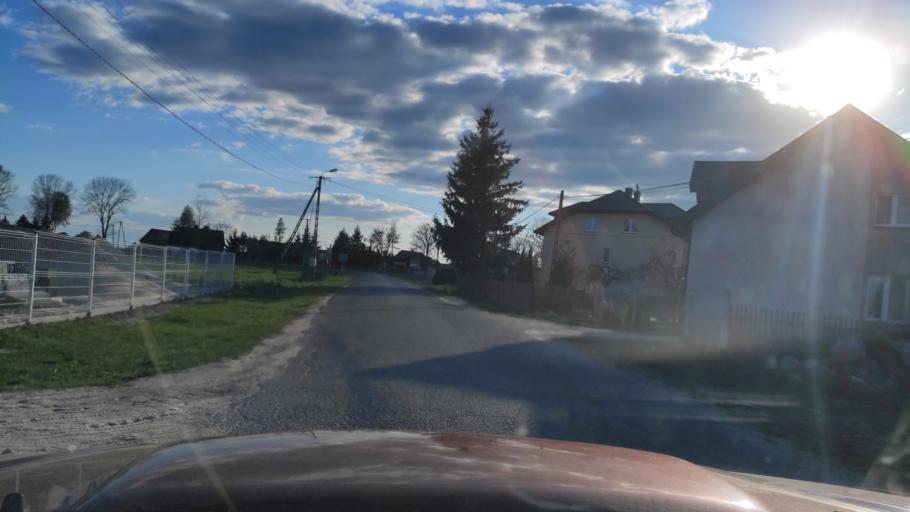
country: PL
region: Masovian Voivodeship
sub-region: Powiat zwolenski
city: Zwolen
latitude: 51.3840
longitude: 21.5595
